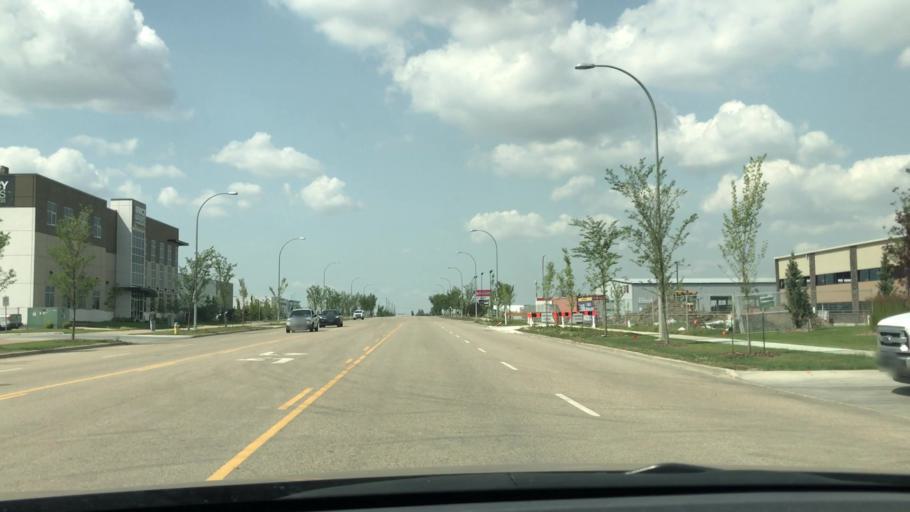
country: CA
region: Alberta
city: Edmonton
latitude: 53.4955
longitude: -113.4078
